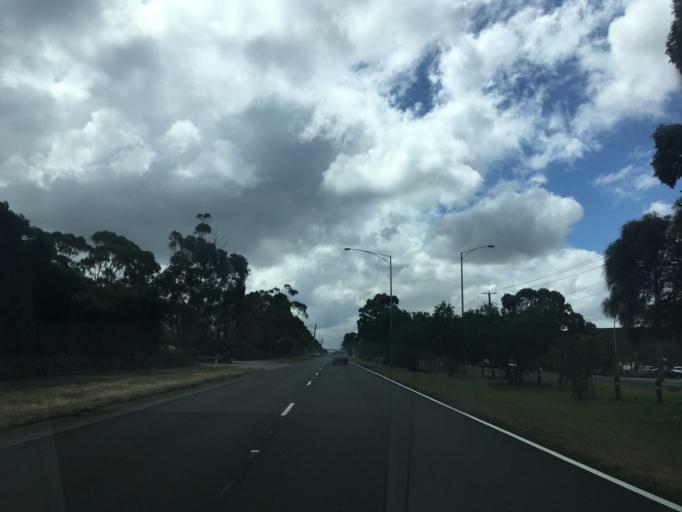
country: AU
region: Victoria
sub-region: Brimbank
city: Derrimut
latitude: -37.8195
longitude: 144.7865
